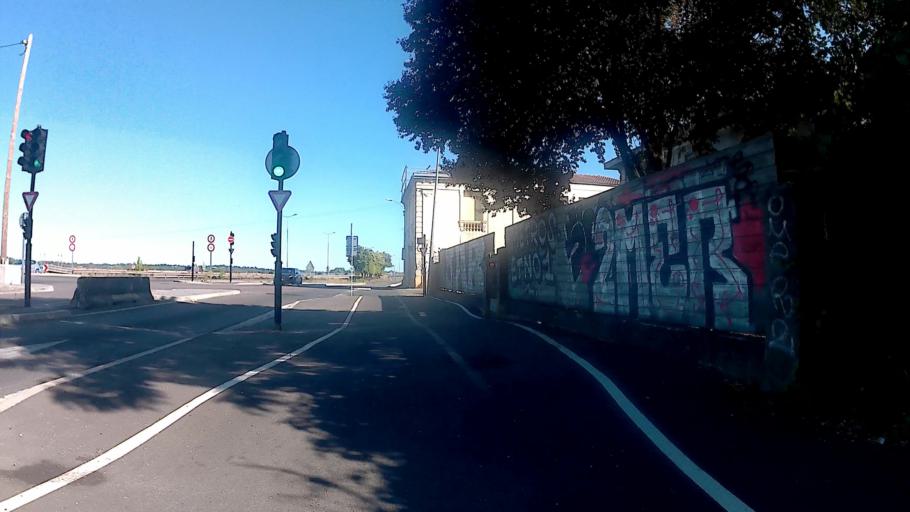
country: FR
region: Aquitaine
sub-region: Departement de la Gironde
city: Begles
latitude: 44.8193
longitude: -0.5389
